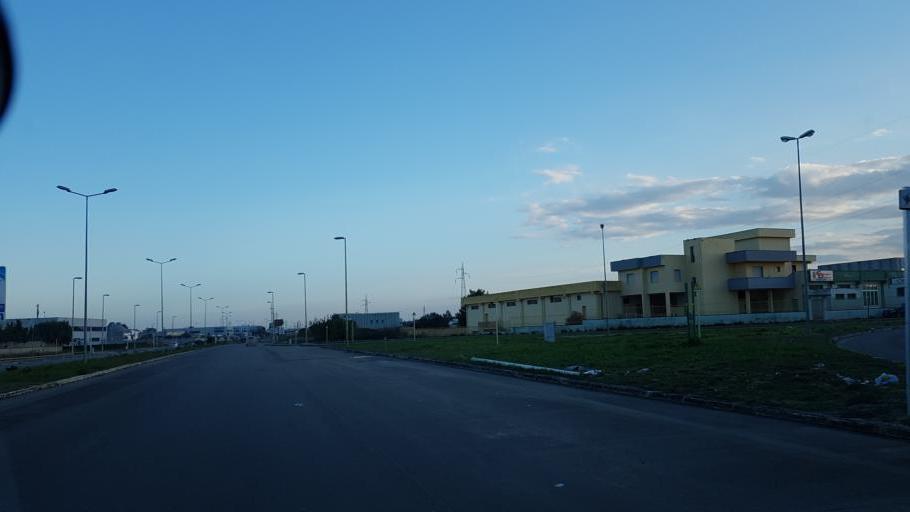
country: IT
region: Apulia
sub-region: Provincia di Lecce
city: Surbo
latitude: 40.3759
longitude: 18.1327
